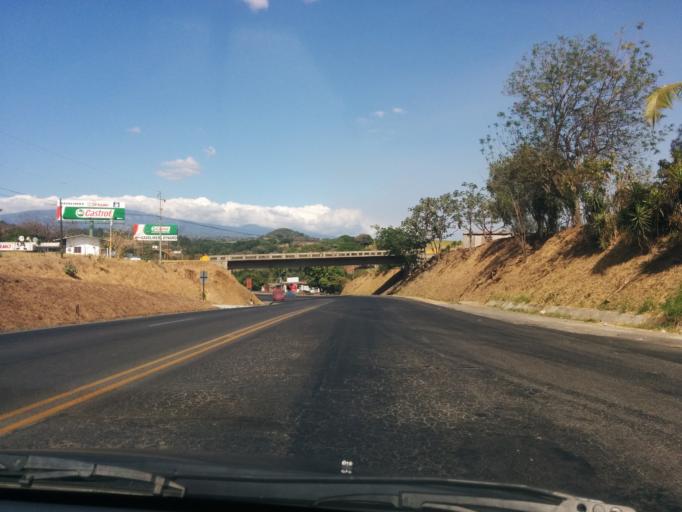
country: CR
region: Alajuela
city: Atenas
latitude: 10.0158
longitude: -84.3423
